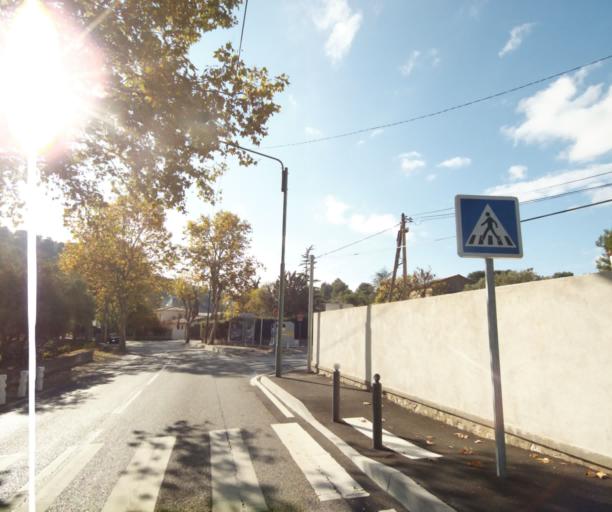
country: FR
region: Provence-Alpes-Cote d'Azur
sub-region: Departement des Bouches-du-Rhone
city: Allauch
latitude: 43.3618
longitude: 5.4939
